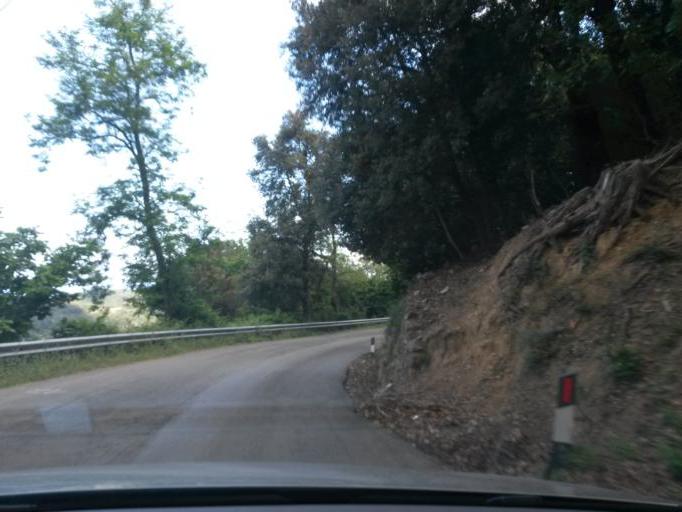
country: IT
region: Tuscany
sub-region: Provincia di Livorno
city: Marciana
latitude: 42.7897
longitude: 10.1824
